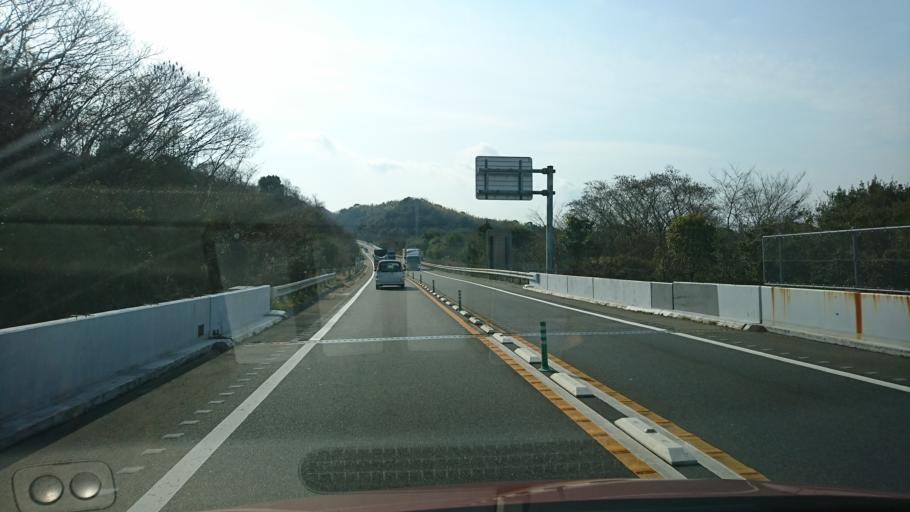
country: JP
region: Hiroshima
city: Onomichi
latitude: 34.3755
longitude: 133.1912
